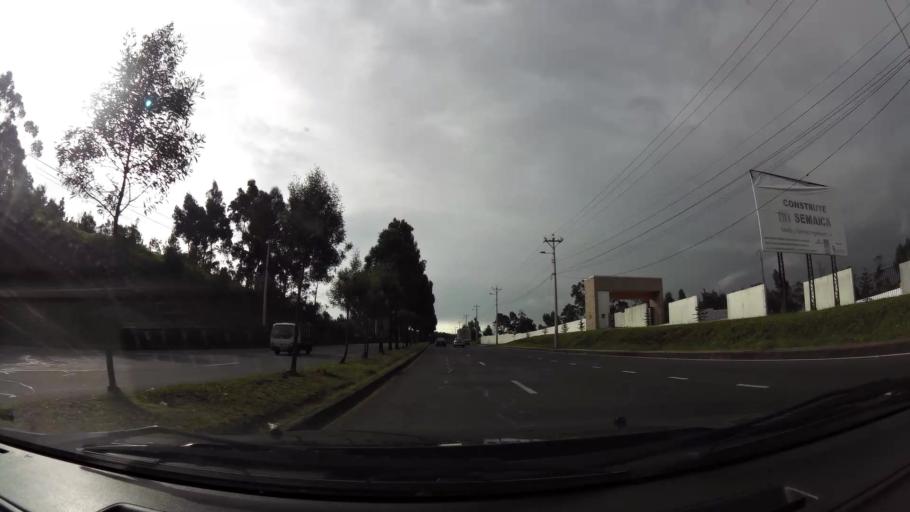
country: EC
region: Pichincha
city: Sangolqui
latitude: -0.3502
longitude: -78.5230
